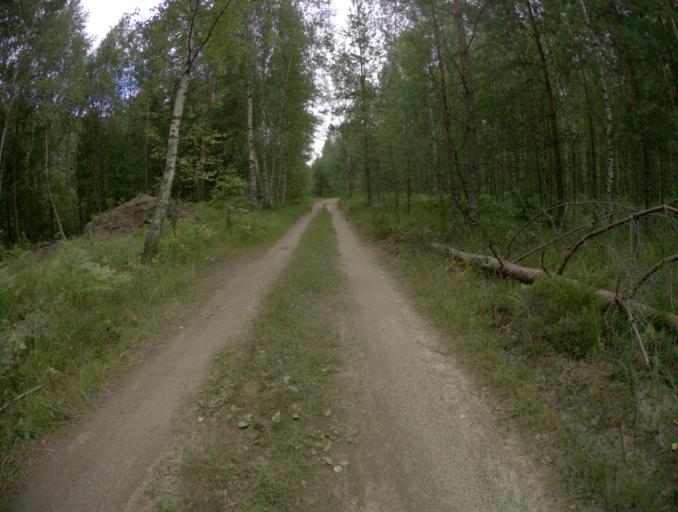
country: RU
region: Vladimir
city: Raduzhnyy
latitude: 55.9686
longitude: 40.2575
